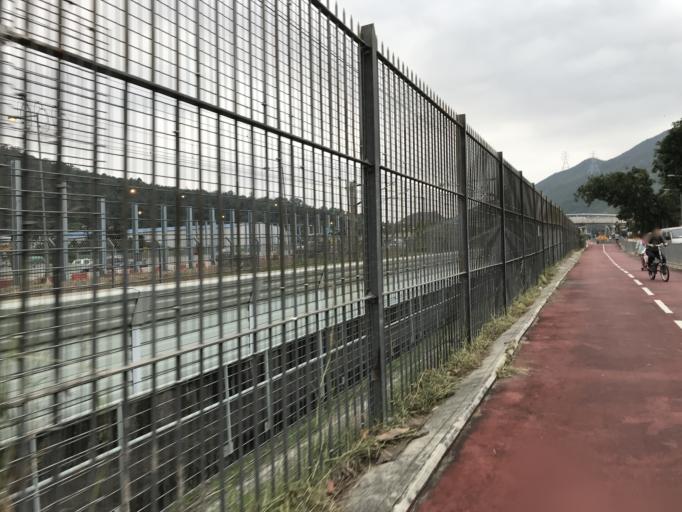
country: HK
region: Tai Po
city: Tai Po
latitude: 22.4723
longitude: 114.1539
